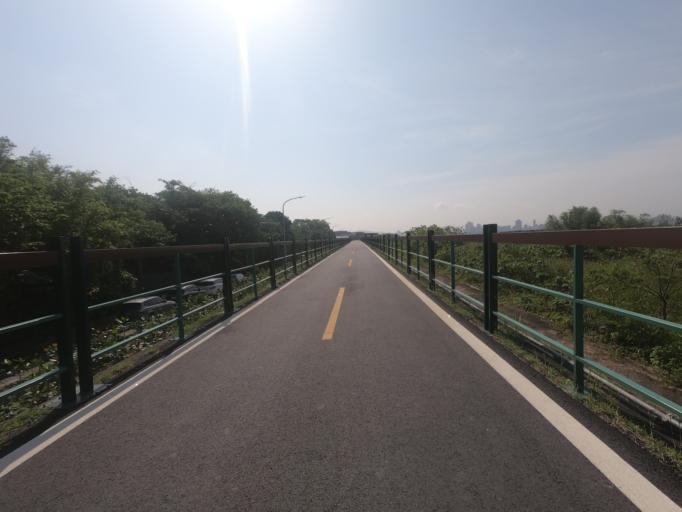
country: TW
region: Taipei
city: Taipei
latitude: 25.1081
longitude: 121.4678
